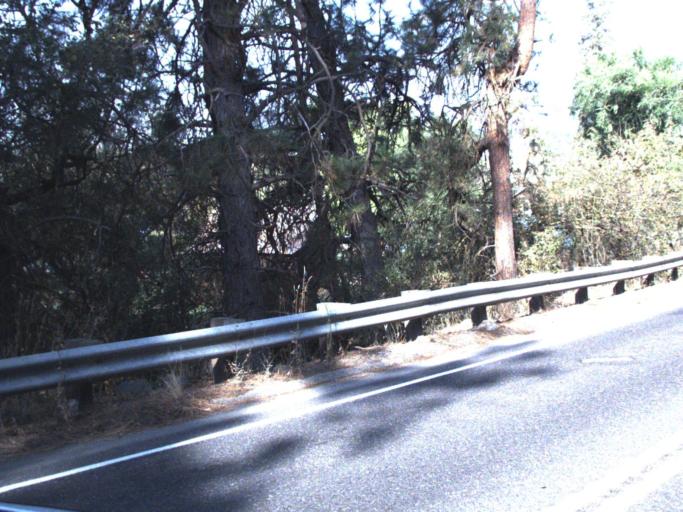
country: US
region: Washington
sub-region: Spokane County
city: Fairwood
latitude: 47.8012
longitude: -117.5437
